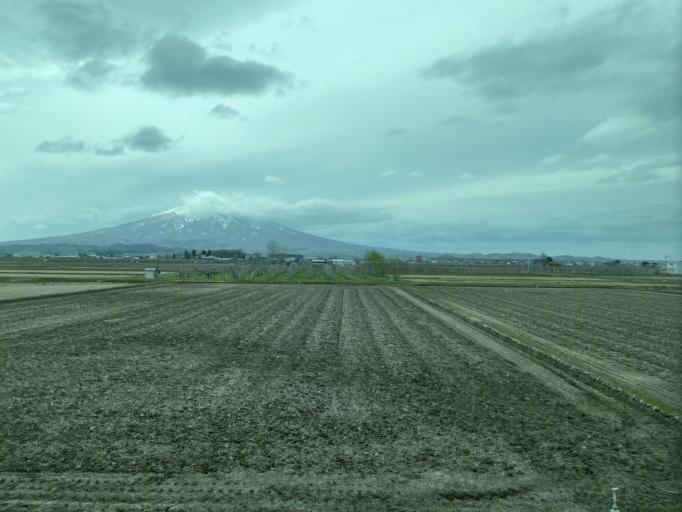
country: JP
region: Aomori
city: Goshogawara
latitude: 40.7220
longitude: 140.4427
